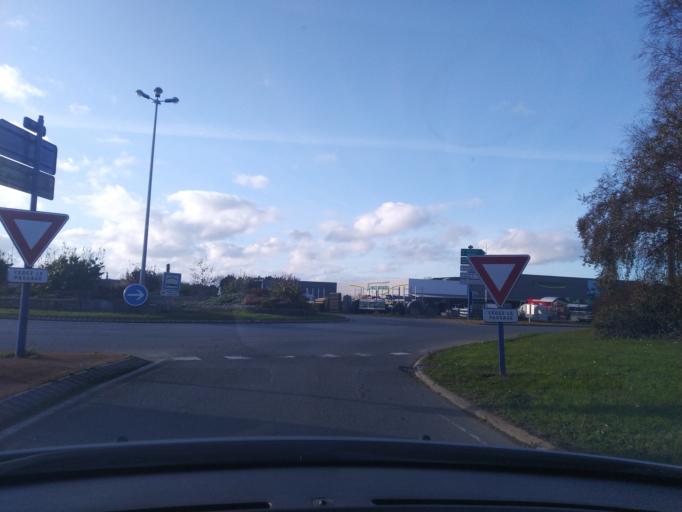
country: FR
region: Brittany
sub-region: Departement du Finistere
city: Plouigneau
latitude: 48.5712
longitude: -3.7200
